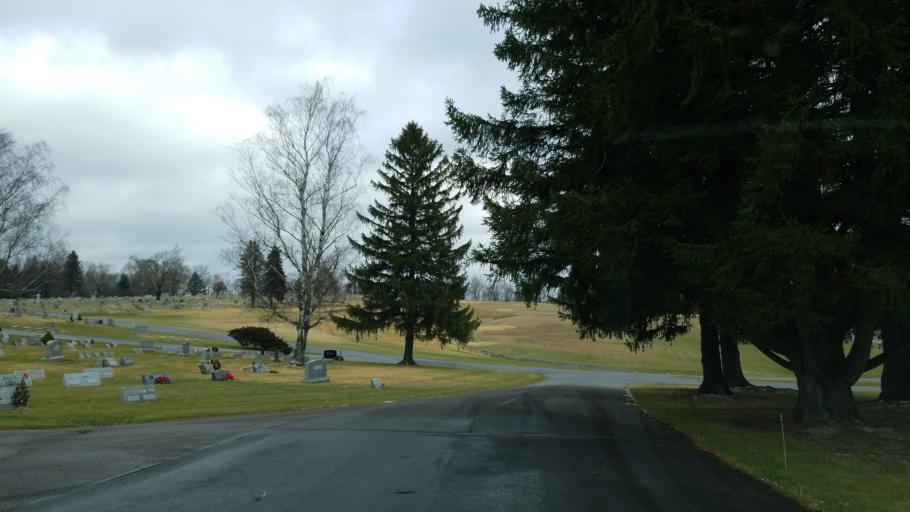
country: US
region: Pennsylvania
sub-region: Clearfield County
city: DuBois
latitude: 41.1240
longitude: -78.7206
